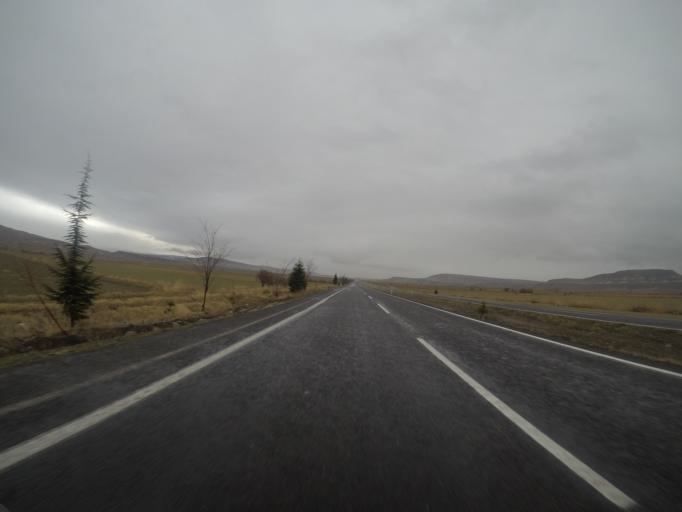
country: TR
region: Nevsehir
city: Urgub
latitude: 38.7209
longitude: 34.9464
